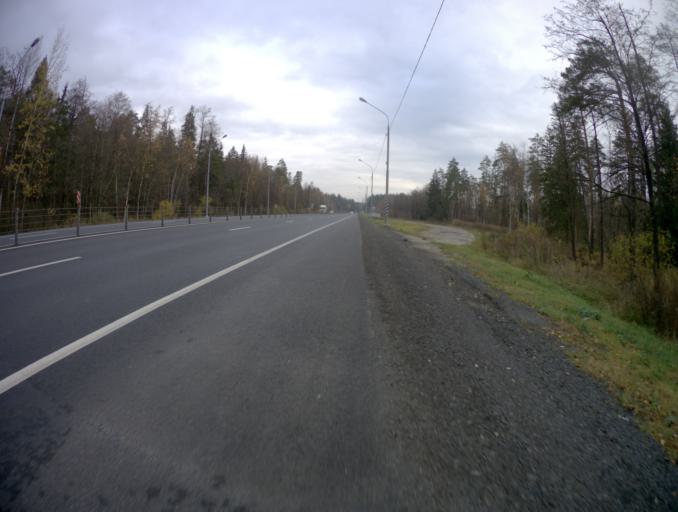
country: RU
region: Moskovskaya
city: Malaya Dubna
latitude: 55.8585
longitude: 38.9626
